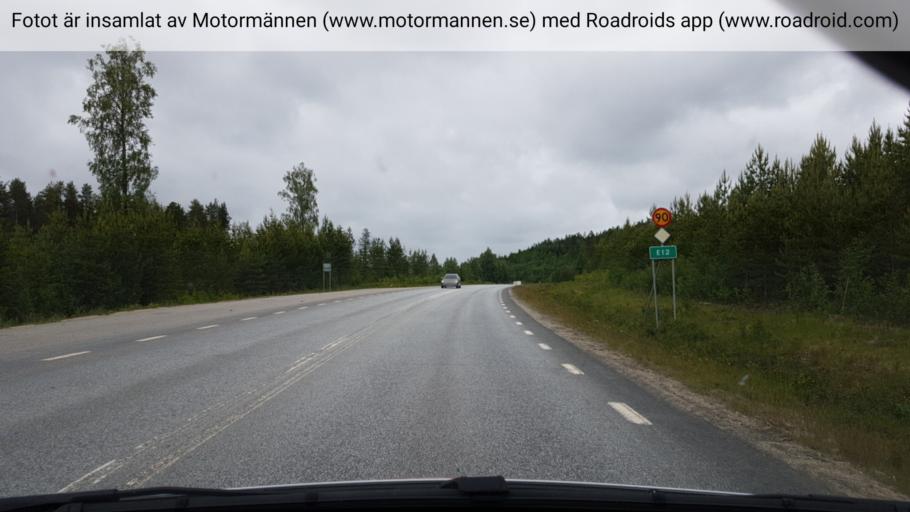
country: SE
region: Vaesterbotten
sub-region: Vannas Kommun
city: Vaennaes
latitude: 63.9850
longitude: 19.7294
